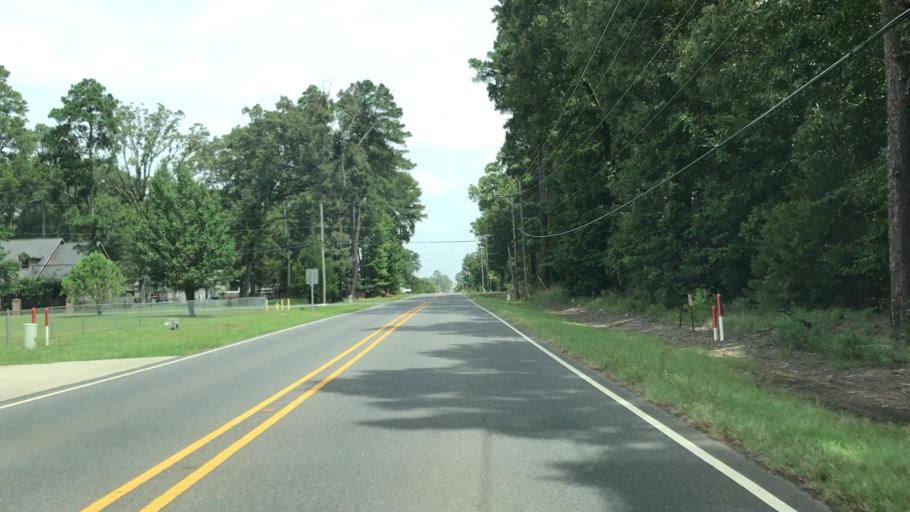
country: US
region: Louisiana
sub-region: De Soto Parish
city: Stonewall
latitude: 32.3830
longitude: -93.7634
